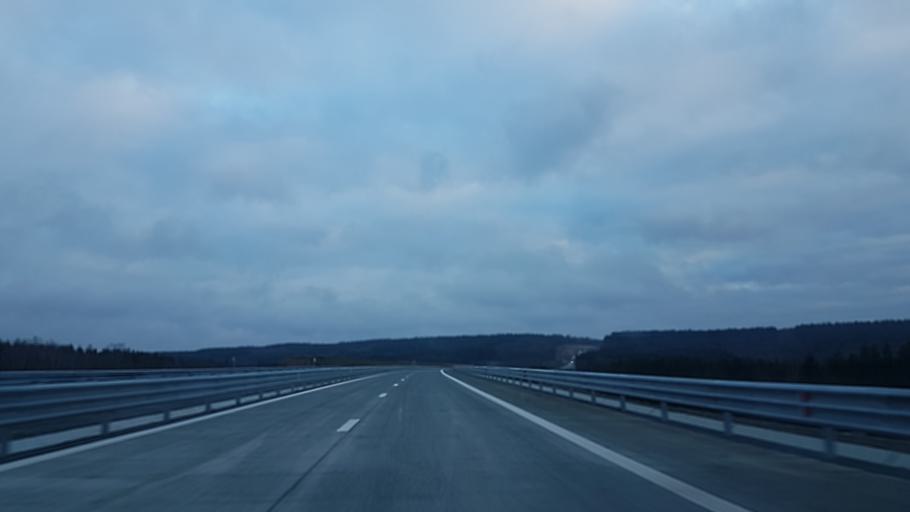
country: BE
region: Wallonia
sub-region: Province de Namur
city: Couvin
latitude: 50.0157
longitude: 4.5315
